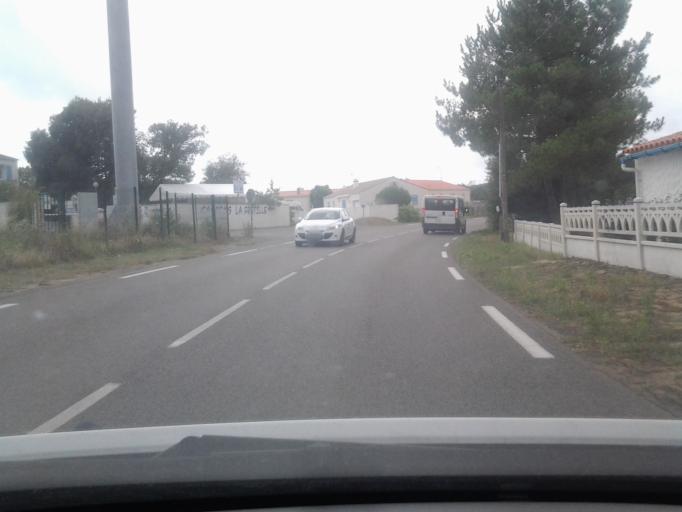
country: FR
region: Pays de la Loire
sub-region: Departement de la Vendee
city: Longeville-sur-Mer
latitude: 46.3930
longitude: -1.4820
